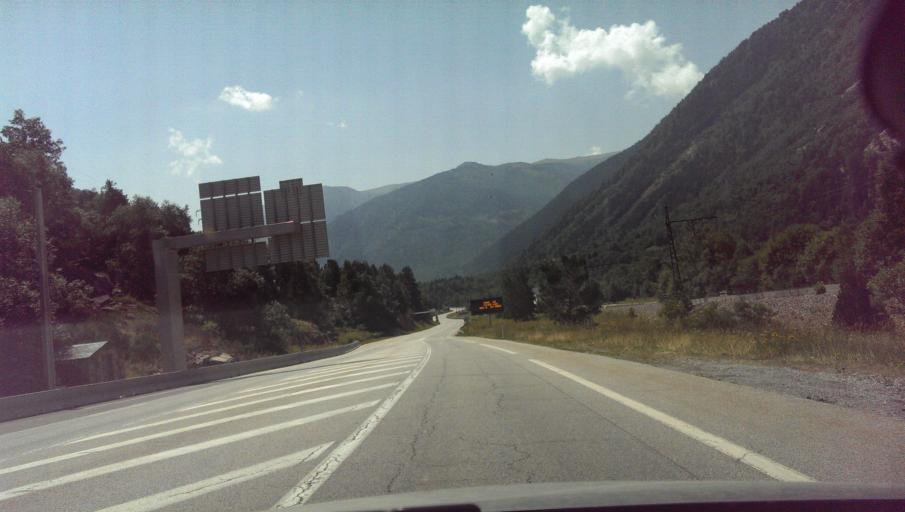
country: AD
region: Encamp
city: Pas de la Casa
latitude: 42.5365
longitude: 1.8235
